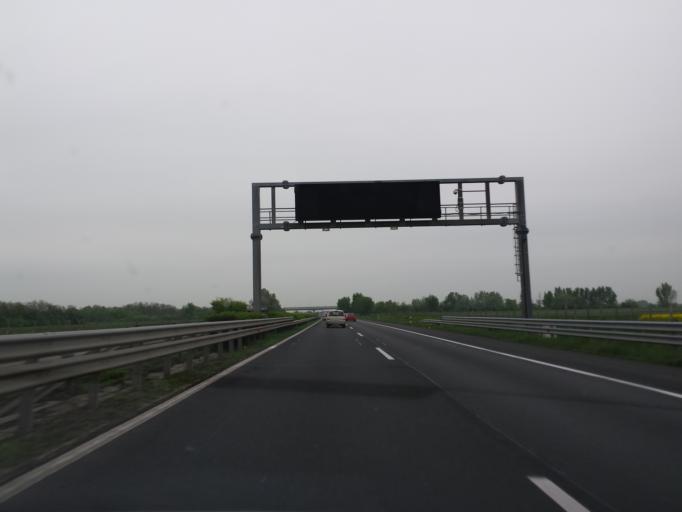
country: HU
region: Gyor-Moson-Sopron
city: Mosonmagyarovar
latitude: 47.8308
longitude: 17.2762
